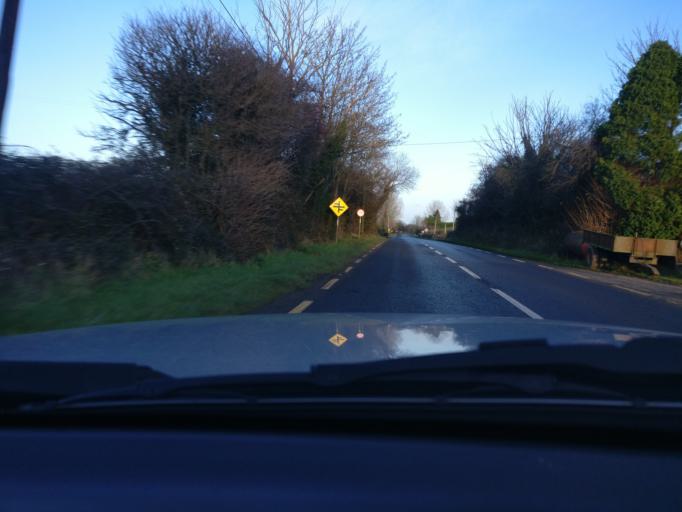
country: IE
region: Leinster
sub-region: Lu
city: Ardee
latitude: 53.8268
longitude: -6.6323
